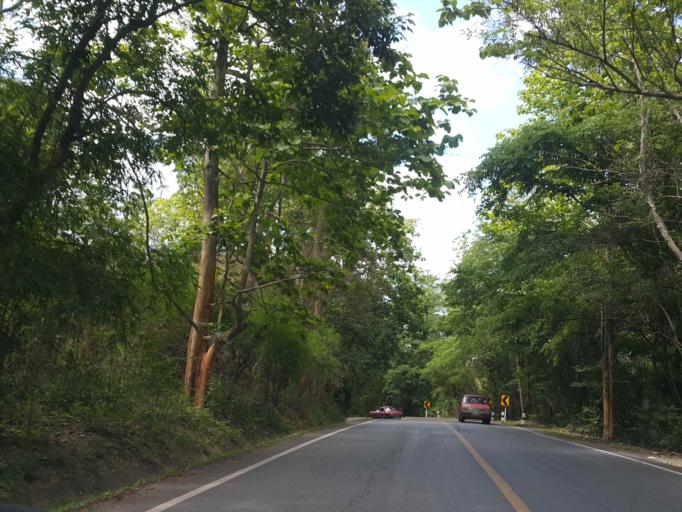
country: TH
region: Chiang Mai
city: Chiang Mai
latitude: 18.9037
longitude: 98.8881
